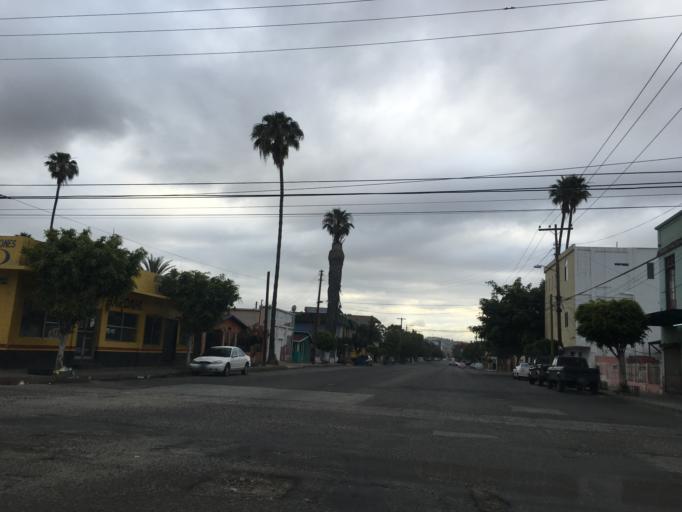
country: MX
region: Baja California
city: Tijuana
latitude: 32.5369
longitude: -117.0495
